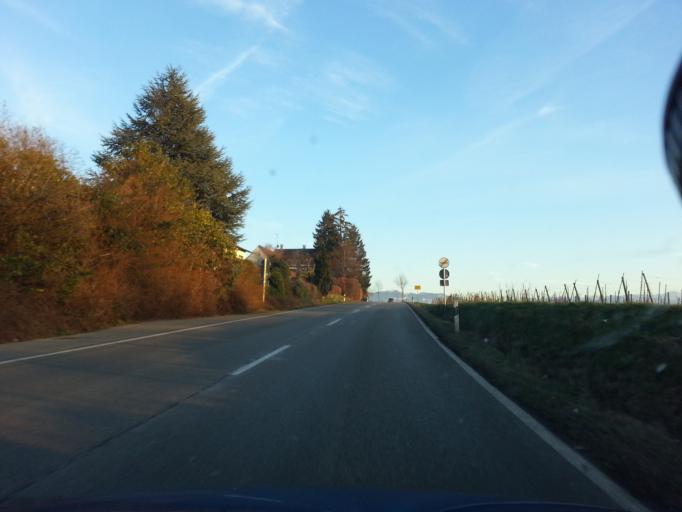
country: DE
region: Bavaria
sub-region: Swabia
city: Bodolz
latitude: 47.5671
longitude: 9.6605
